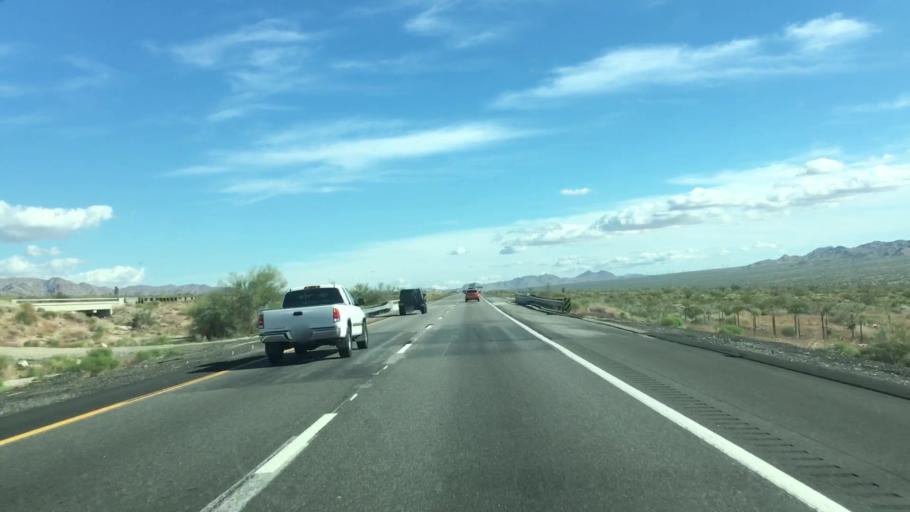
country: US
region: California
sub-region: Riverside County
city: Mecca
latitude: 33.6647
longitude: -115.8800
